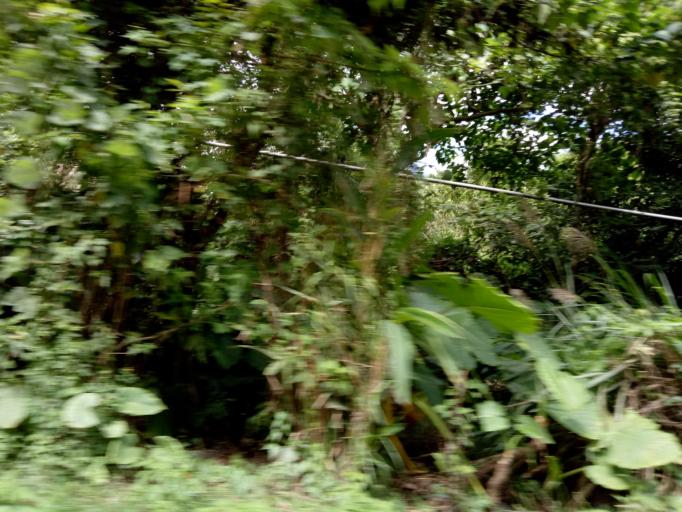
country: TW
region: Taiwan
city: Daxi
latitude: 24.8940
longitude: 121.2815
